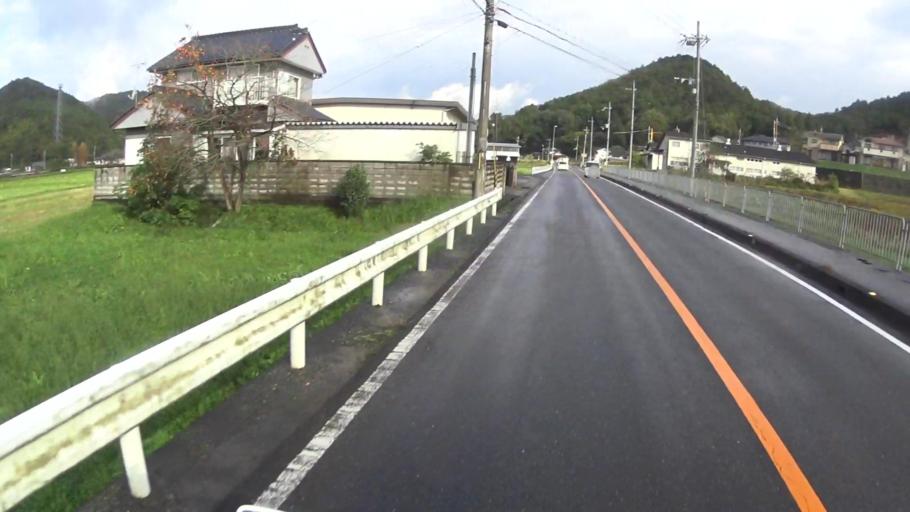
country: JP
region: Kyoto
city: Ayabe
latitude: 35.3304
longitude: 135.2151
